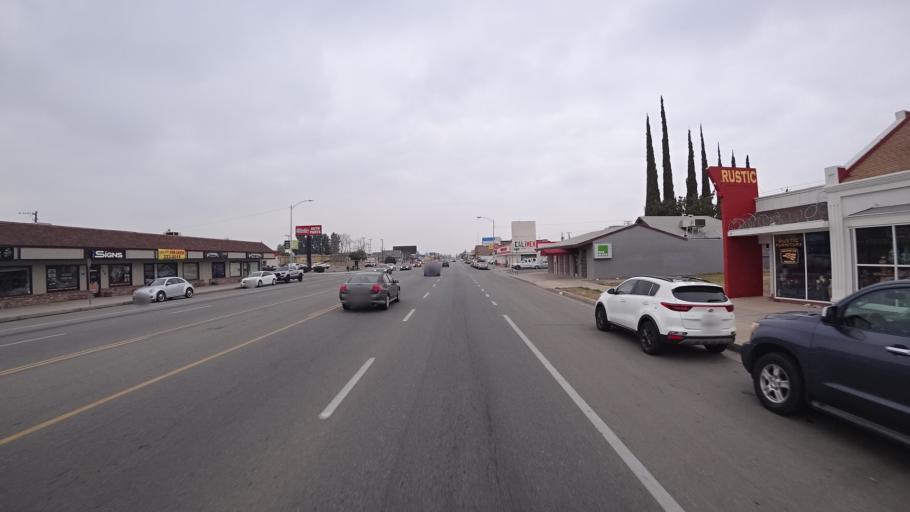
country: US
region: California
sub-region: Kern County
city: Bakersfield
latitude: 35.3594
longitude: -119.0190
